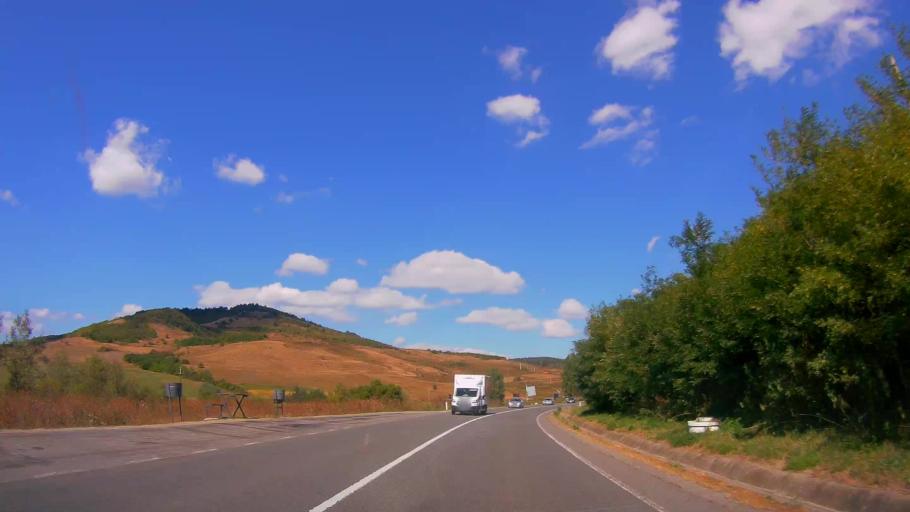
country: RO
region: Cluj
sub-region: Comuna Sanpaul
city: Sanpaul
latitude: 46.8577
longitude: 23.4062
